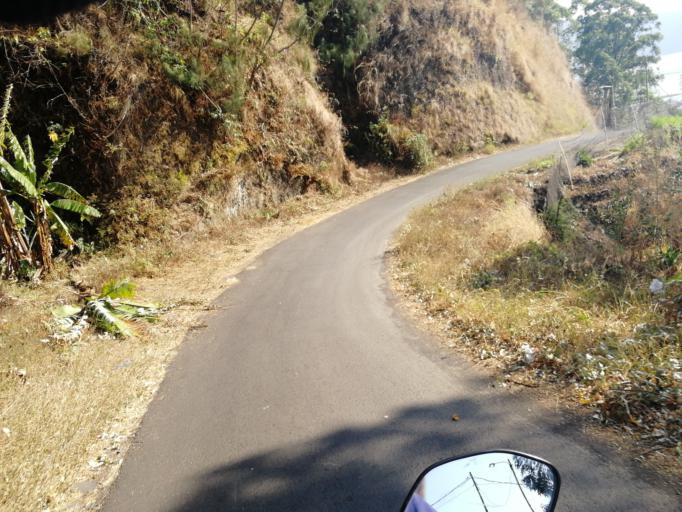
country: ID
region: Bali
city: Banjar Trunyan
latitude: -8.2563
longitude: 115.4242
